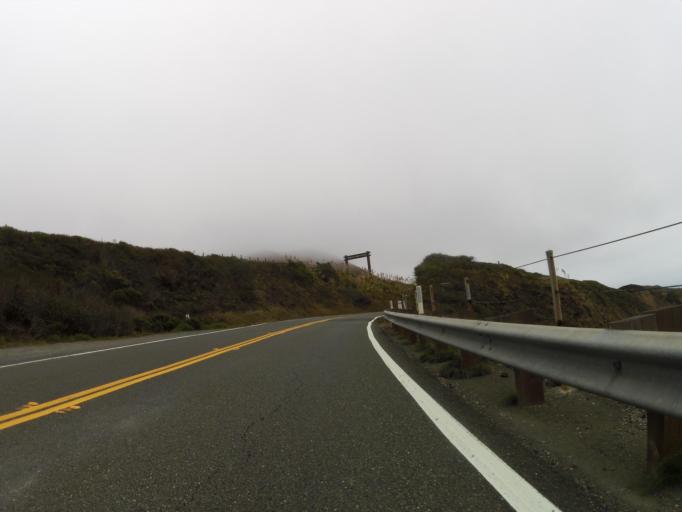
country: US
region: California
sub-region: Sonoma County
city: Monte Rio
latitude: 38.4656
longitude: -123.1526
